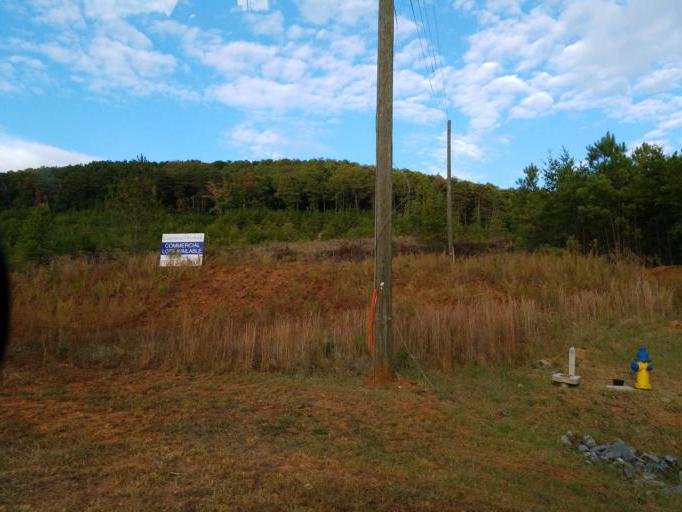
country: US
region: Georgia
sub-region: Bartow County
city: Cartersville
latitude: 34.1757
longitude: -84.7558
